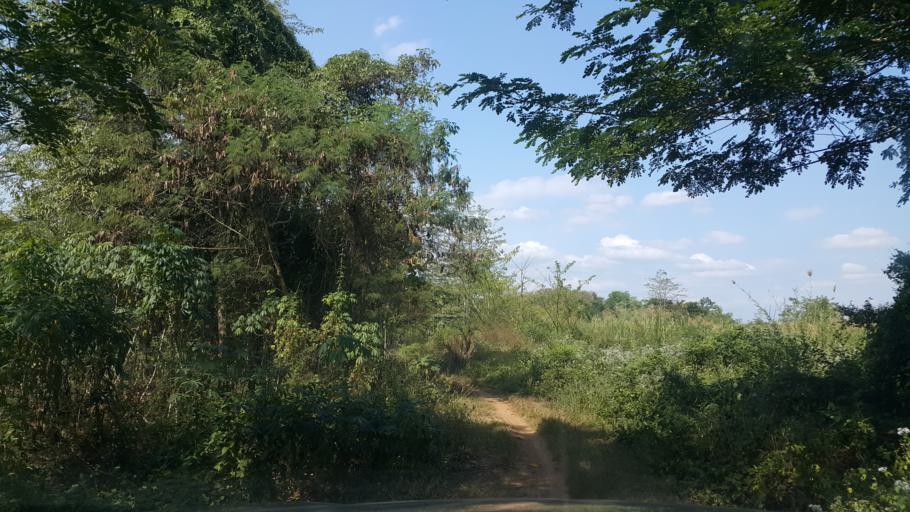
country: TH
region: Sukhothai
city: Thung Saliam
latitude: 17.3264
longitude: 99.5830
